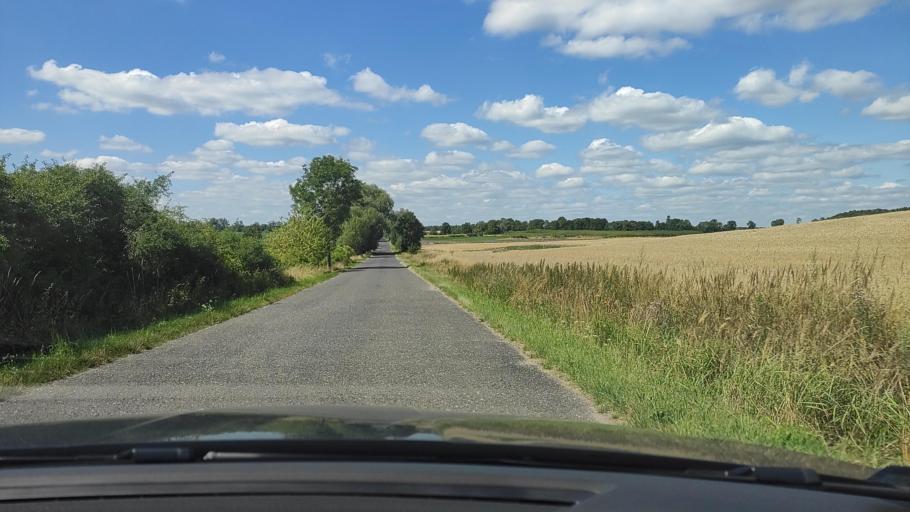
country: PL
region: Greater Poland Voivodeship
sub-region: Powiat poznanski
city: Kobylnica
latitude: 52.4905
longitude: 17.1325
